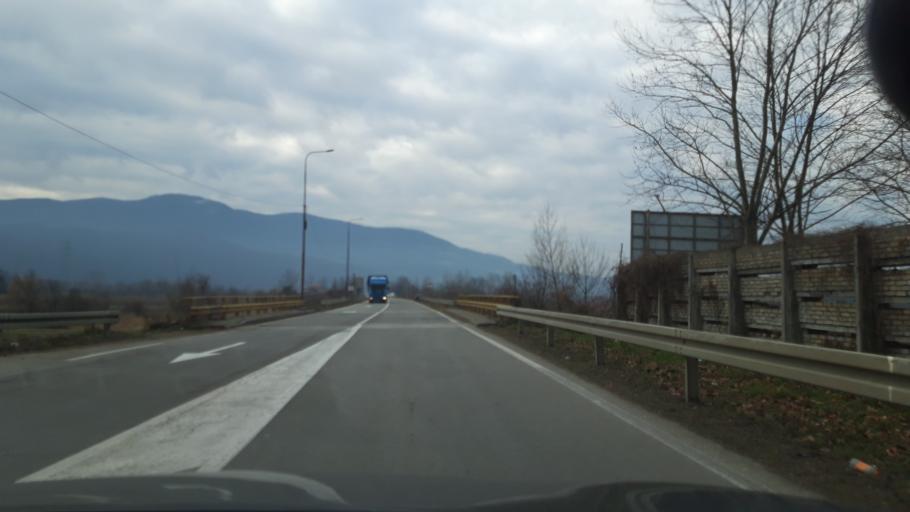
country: RS
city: Trsic
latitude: 44.5356
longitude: 19.1825
